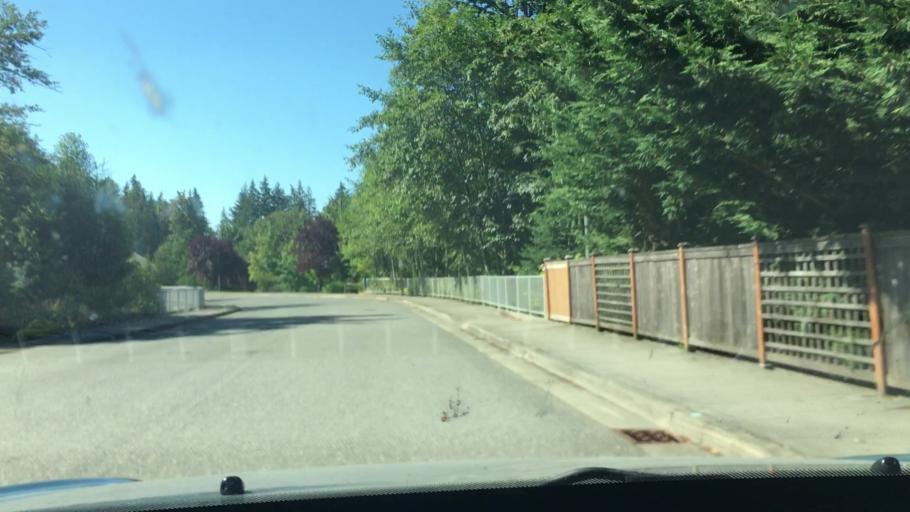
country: US
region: Washington
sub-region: King County
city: Newcastle
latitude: 47.5412
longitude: -122.1198
